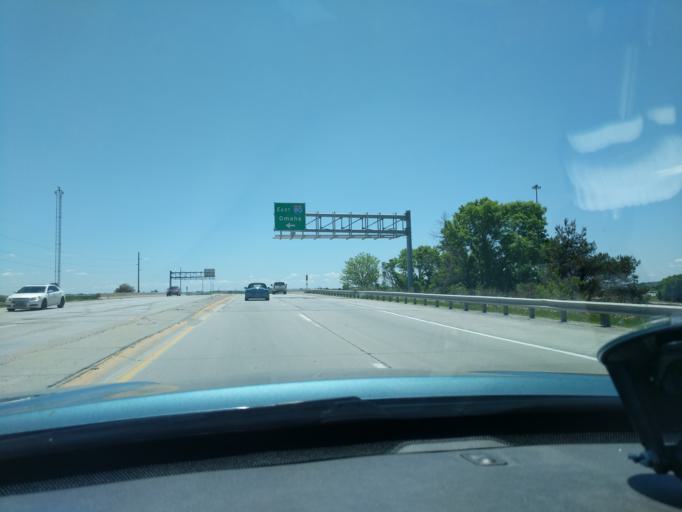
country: US
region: Nebraska
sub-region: Sarpy County
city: Chalco
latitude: 41.1630
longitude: -96.1388
